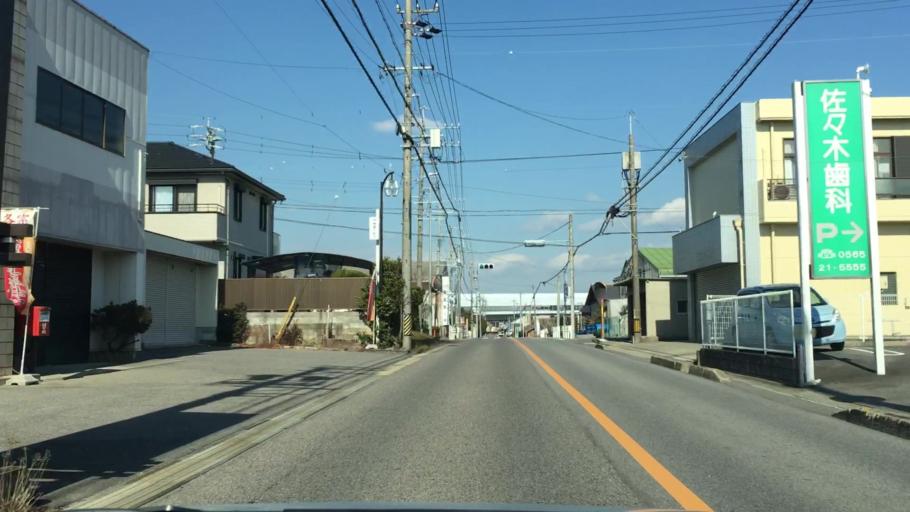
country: JP
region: Aichi
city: Anjo
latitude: 35.0101
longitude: 137.1209
